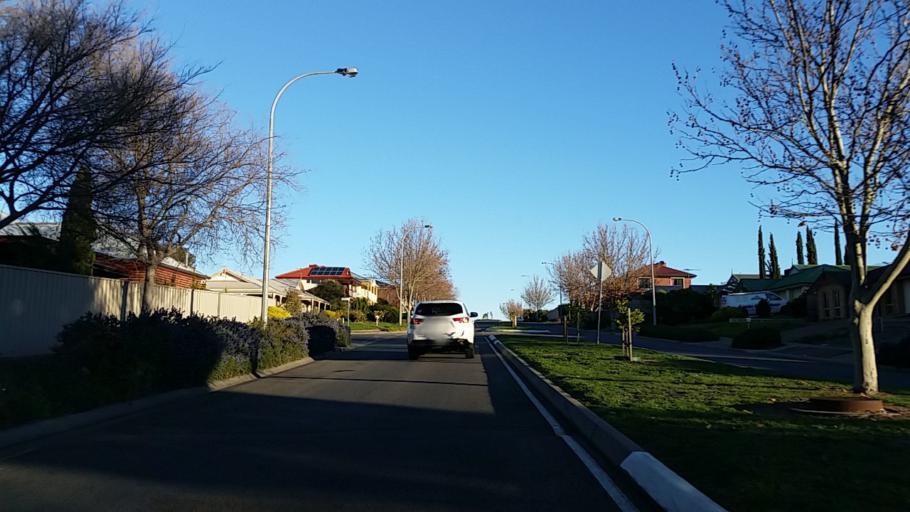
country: AU
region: South Australia
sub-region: Onkaparinga
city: Moana
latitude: -35.2016
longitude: 138.4876
